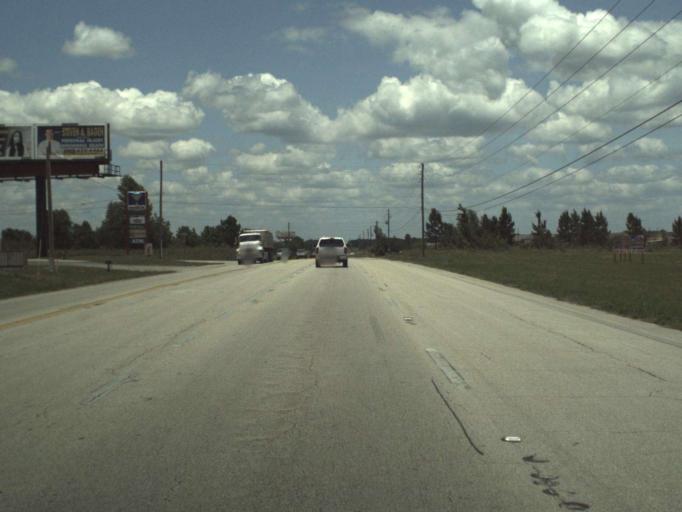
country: US
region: Florida
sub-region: Marion County
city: Silver Springs Shores
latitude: 29.1034
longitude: -82.0535
